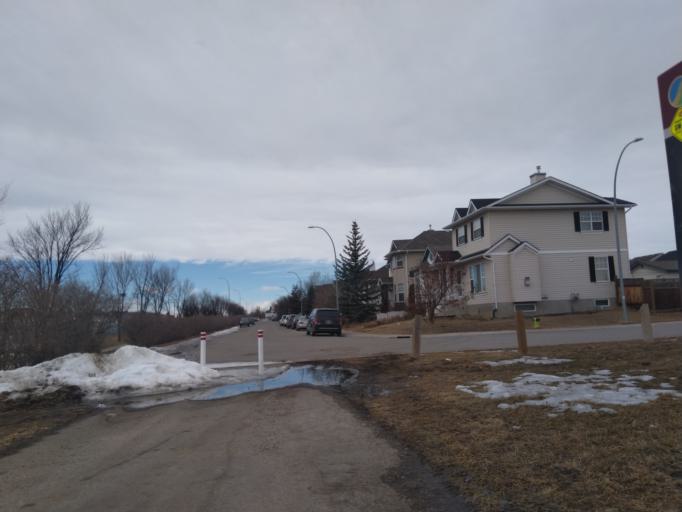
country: CA
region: Alberta
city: Chestermere
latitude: 51.1109
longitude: -113.9291
